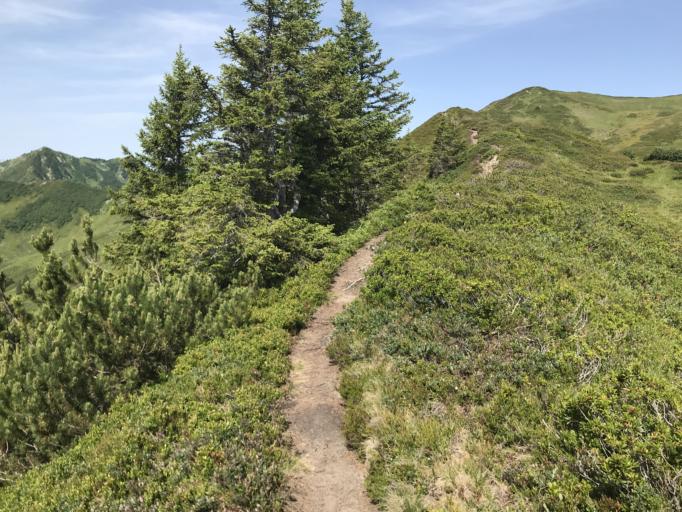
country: AT
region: Vorarlberg
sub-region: Politischer Bezirk Bregenz
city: Damuels
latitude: 47.2861
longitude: 9.8558
